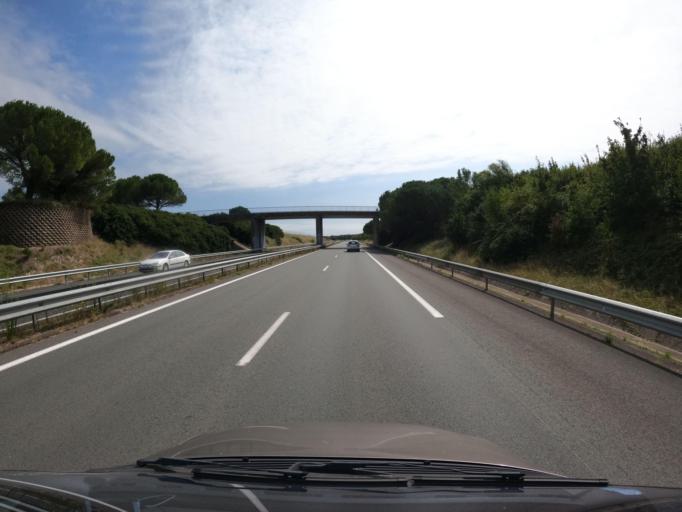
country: FR
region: Poitou-Charentes
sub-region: Departement de la Charente-Maritime
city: Saint-Jean-de-Liversay
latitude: 46.2245
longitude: -0.8604
